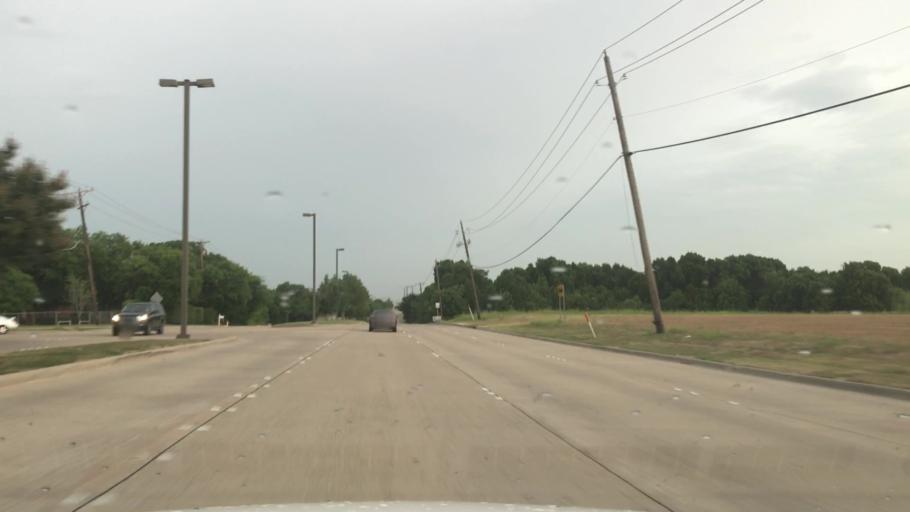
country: US
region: Texas
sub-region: Dallas County
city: Mesquite
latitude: 32.7304
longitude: -96.5540
